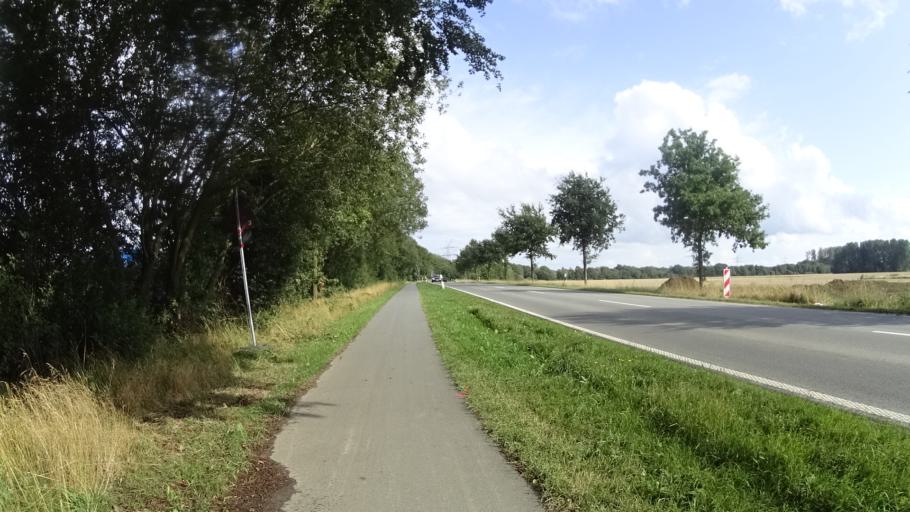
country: DE
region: Lower Saxony
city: Bockhorn
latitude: 53.3917
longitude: 7.9991
